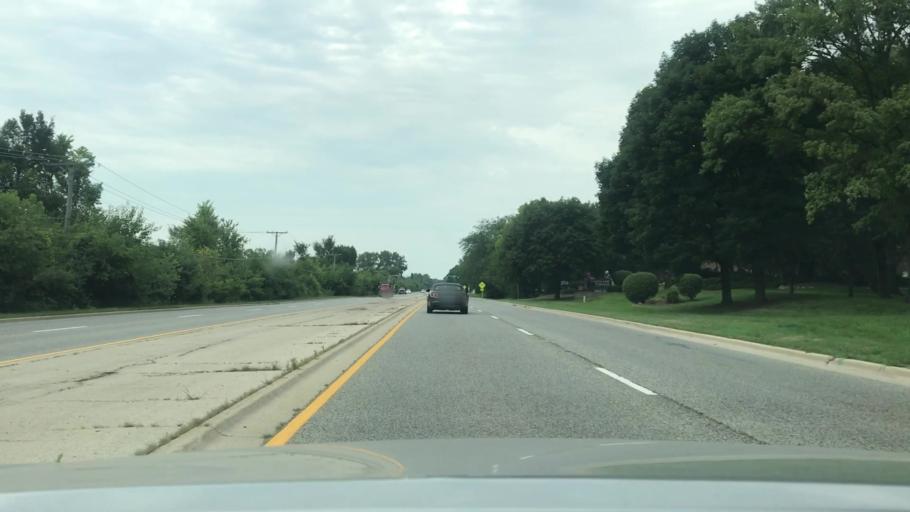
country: US
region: Illinois
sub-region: DuPage County
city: Woodridge
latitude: 41.7327
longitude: -88.0627
